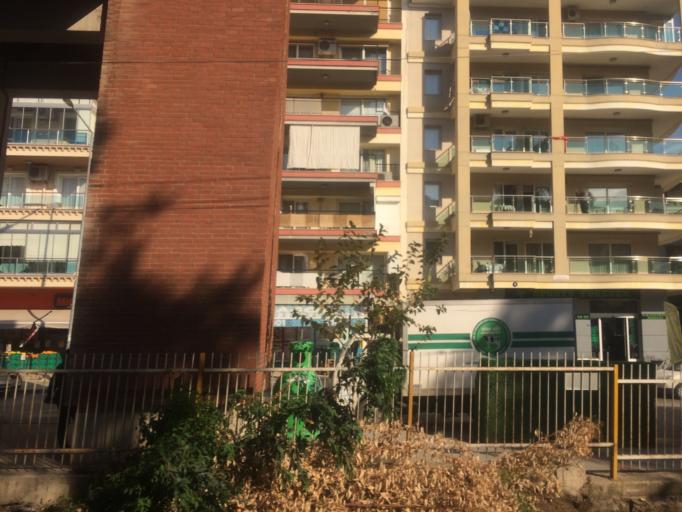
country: TR
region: Izmir
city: Karsiyaka
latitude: 38.4705
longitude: 27.0943
